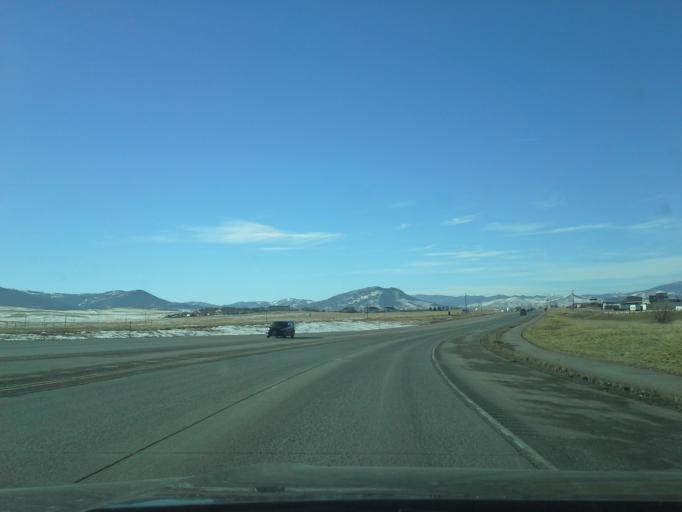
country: US
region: Montana
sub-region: Lewis and Clark County
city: East Helena
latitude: 46.5903
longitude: -111.9508
